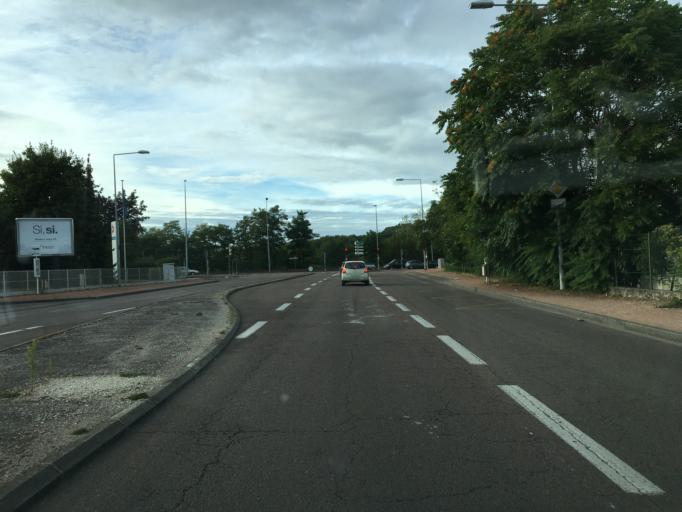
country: FR
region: Bourgogne
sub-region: Departement de la Cote-d'Or
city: Dijon
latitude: 47.3198
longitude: 5.0099
